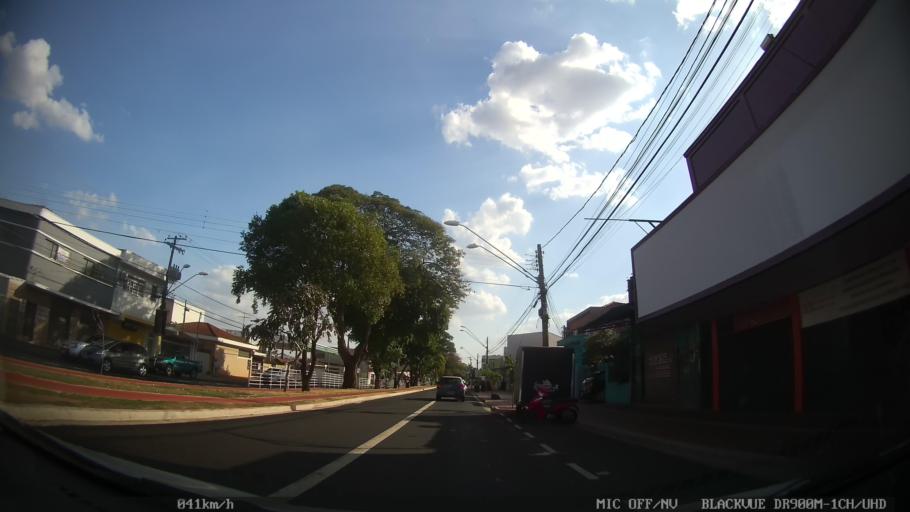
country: BR
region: Sao Paulo
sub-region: Ribeirao Preto
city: Ribeirao Preto
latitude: -21.1744
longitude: -47.8198
